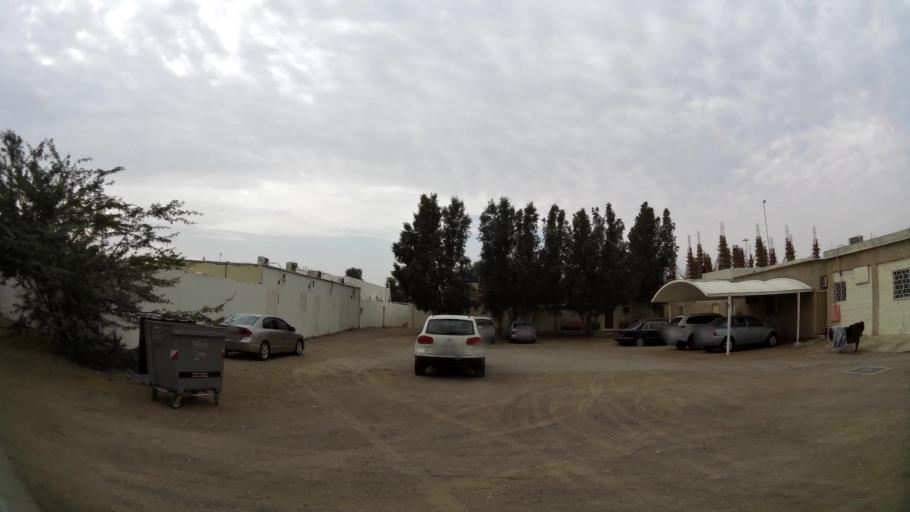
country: AE
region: Abu Dhabi
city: Al Ain
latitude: 24.2259
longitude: 55.7417
